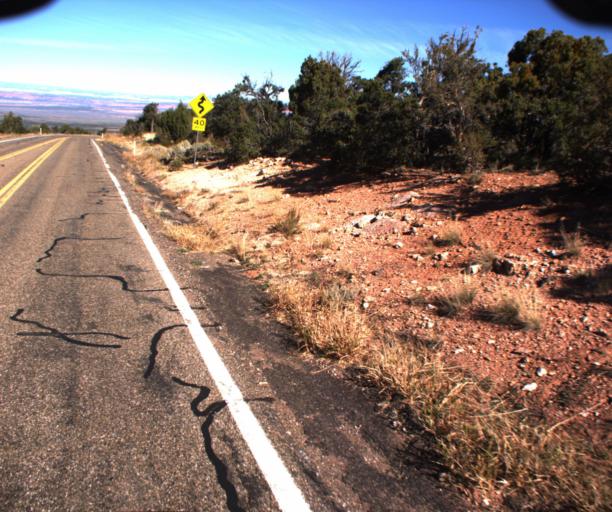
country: US
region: Arizona
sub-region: Coconino County
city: Fredonia
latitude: 36.8305
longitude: -112.2549
